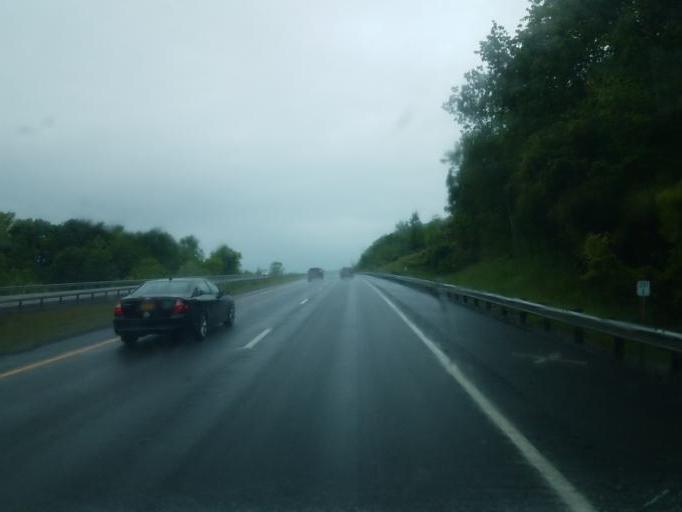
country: US
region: New York
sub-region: Herkimer County
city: Ilion
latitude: 43.0254
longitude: -75.0282
